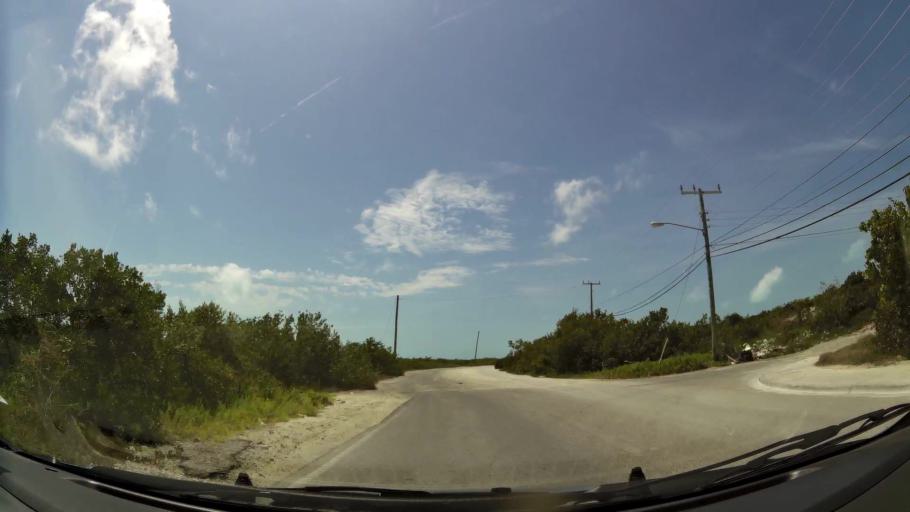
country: BS
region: Mayaguana
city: Abraham's Bay
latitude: 21.7558
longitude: -72.2661
